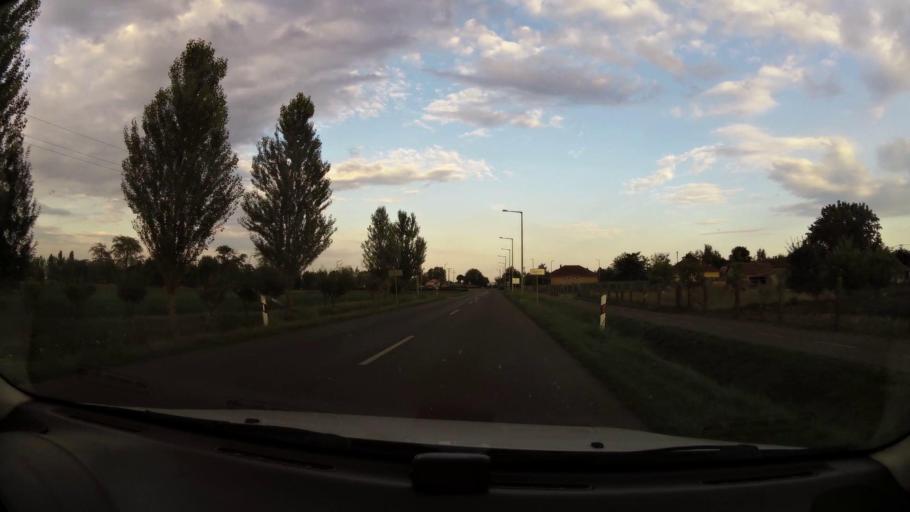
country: HU
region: Pest
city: Ujszilvas
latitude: 47.2791
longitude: 19.9226
